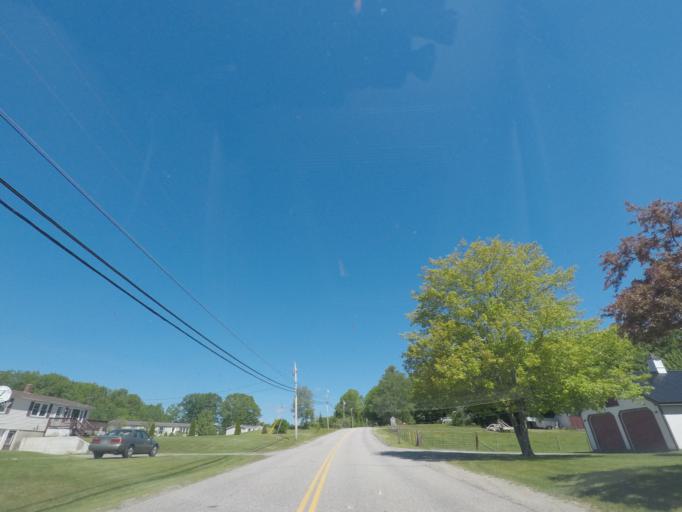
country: US
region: Maine
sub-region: Kennebec County
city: Manchester
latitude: 44.2475
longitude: -69.8981
